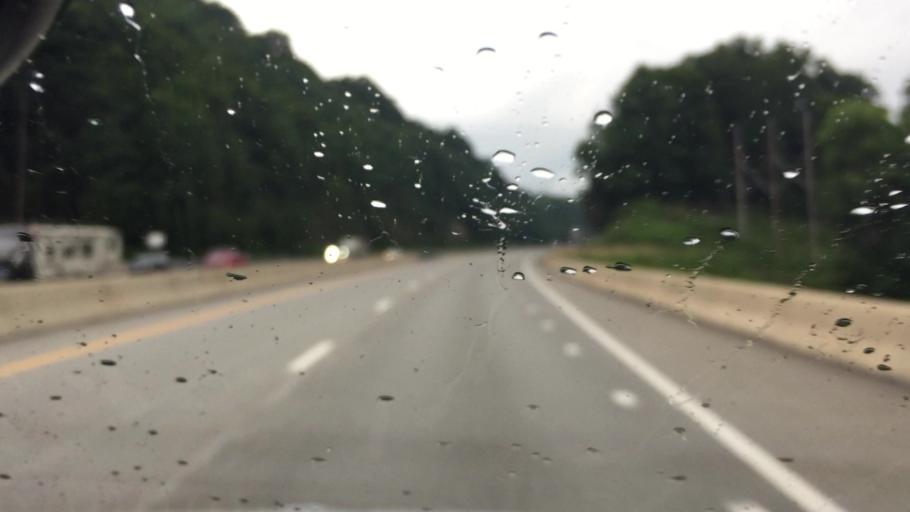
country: US
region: West Virginia
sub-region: Monongalia County
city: Cheat Lake
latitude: 39.6505
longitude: -79.7216
